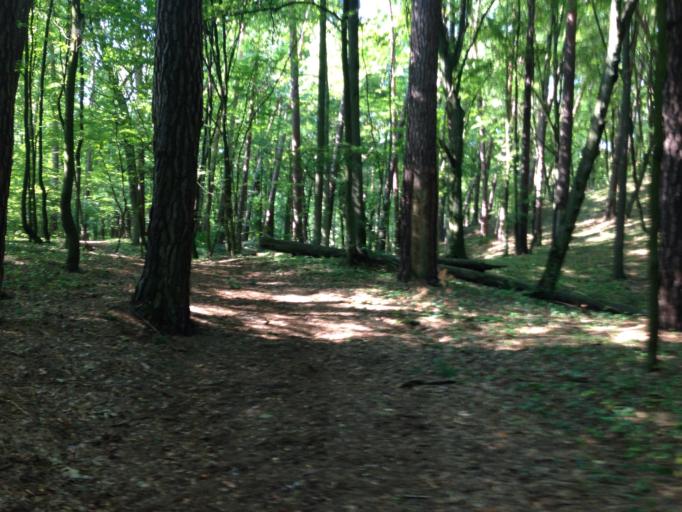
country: PL
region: Kujawsko-Pomorskie
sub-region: Powiat brodnicki
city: Gorzno
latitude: 53.1862
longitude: 19.6542
